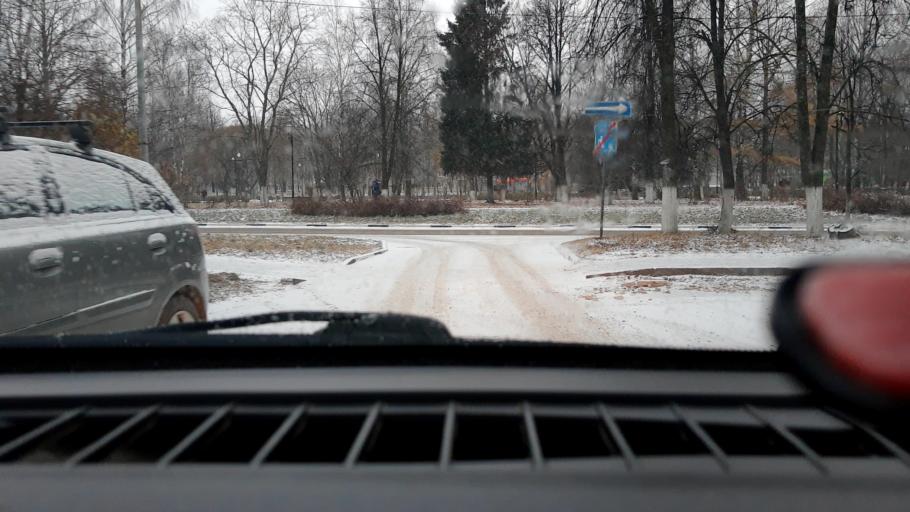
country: RU
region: Nizjnij Novgorod
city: Kstovo
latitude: 56.1457
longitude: 44.2012
